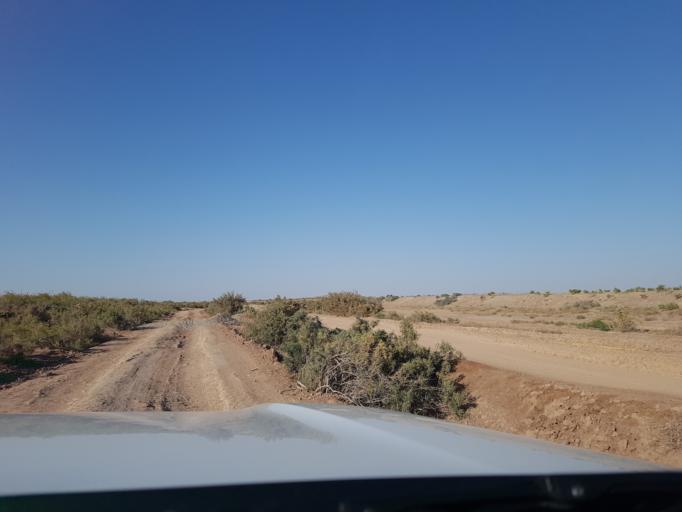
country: IR
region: Razavi Khorasan
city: Sarakhs
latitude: 36.9804
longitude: 61.3857
